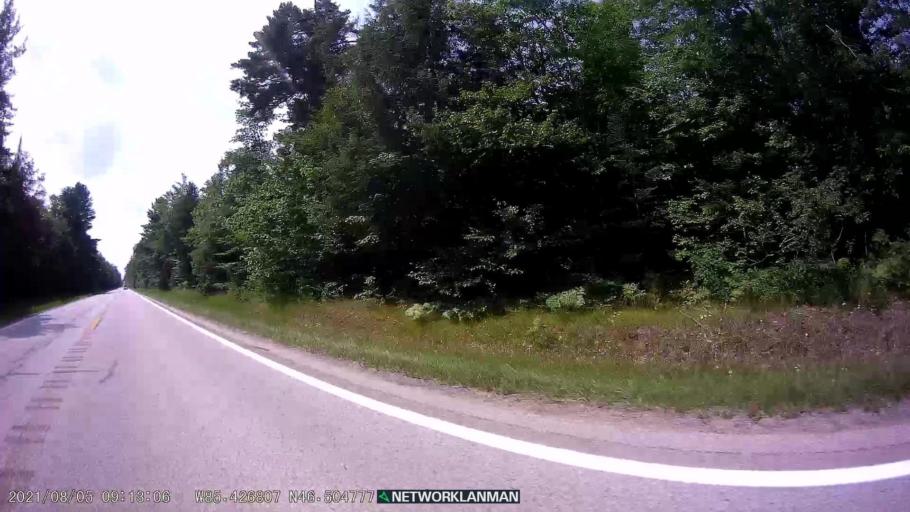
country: US
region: Michigan
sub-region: Luce County
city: Newberry
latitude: 46.5045
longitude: -85.4267
